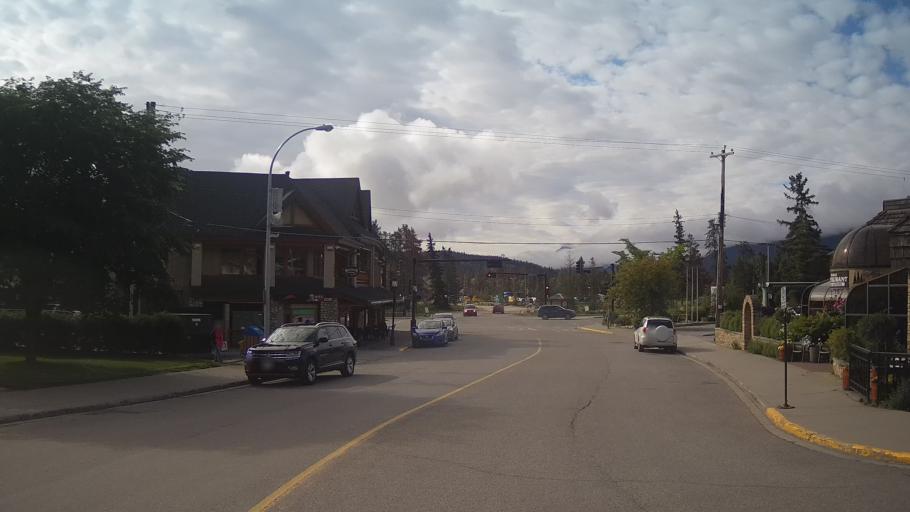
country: CA
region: Alberta
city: Jasper Park Lodge
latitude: 52.8739
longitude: -118.0829
